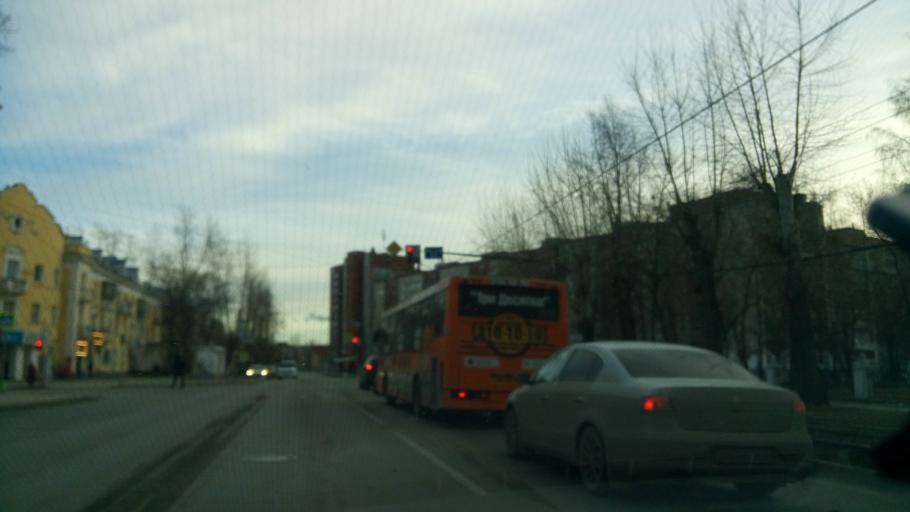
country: RU
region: Sverdlovsk
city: Shuvakish
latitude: 56.8722
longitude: 60.5200
